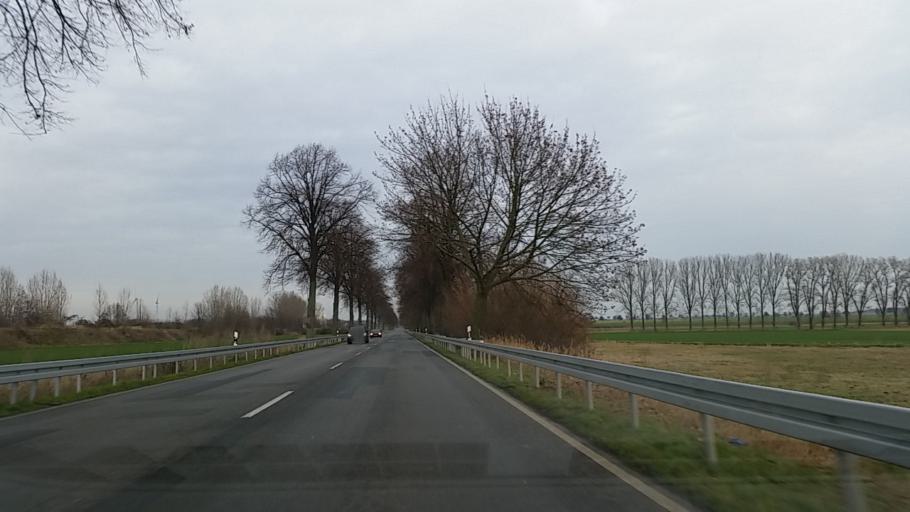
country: DE
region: Lower Saxony
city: Cramme
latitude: 52.1099
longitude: 10.4251
